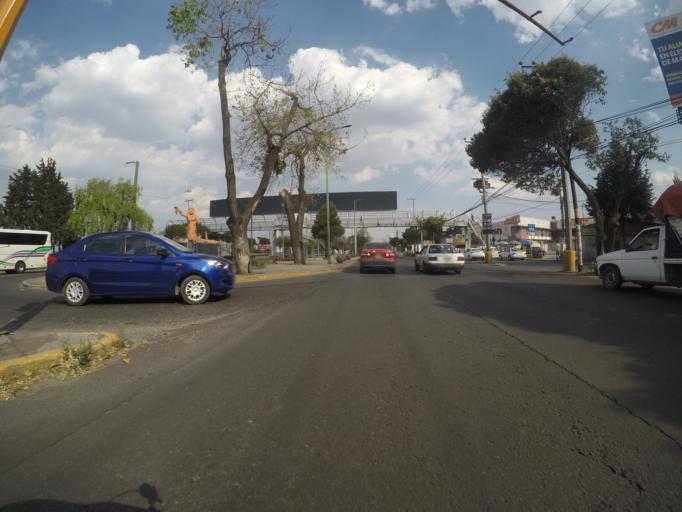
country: MX
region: Mexico
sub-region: Metepec
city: San Jorge Pueblo Nuevo
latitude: 19.2563
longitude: -99.6222
